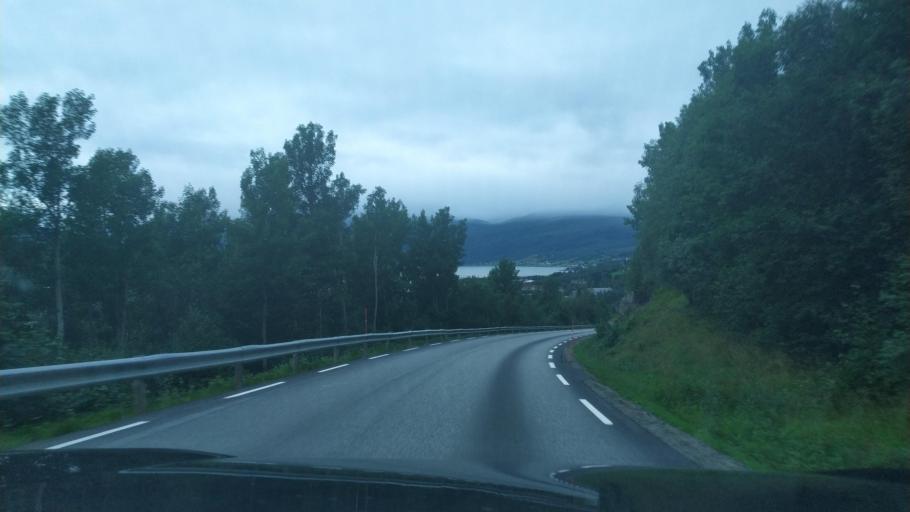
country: NO
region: Troms
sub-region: Lavangen
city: Tennevoll
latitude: 68.7381
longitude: 17.8162
